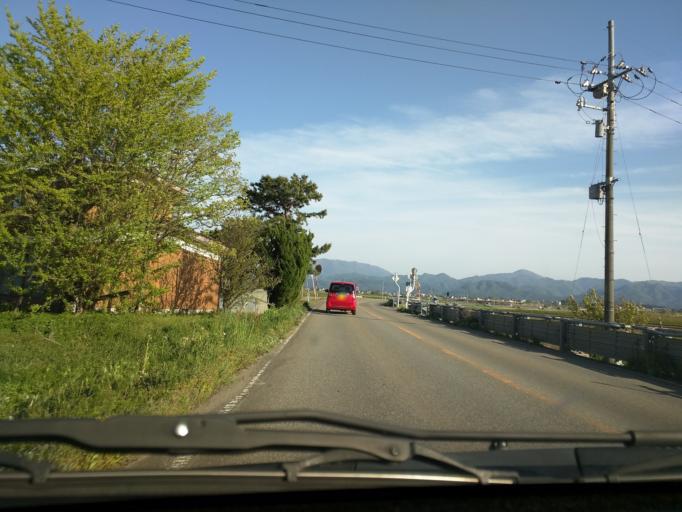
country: JP
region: Fukushima
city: Kitakata
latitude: 37.4852
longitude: 139.8387
